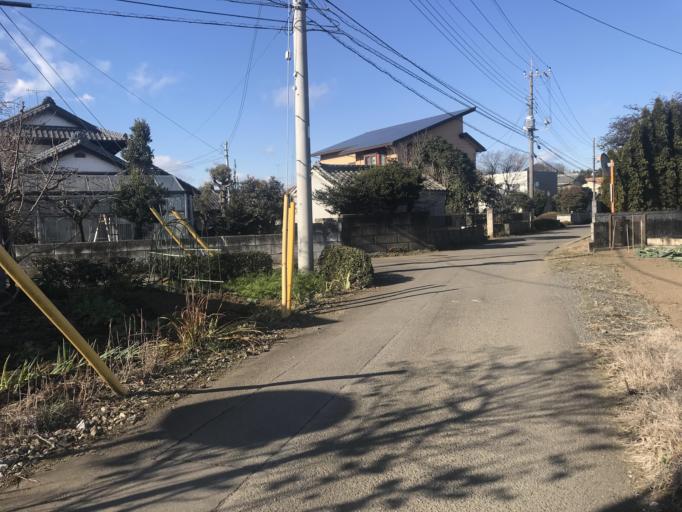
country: JP
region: Tochigi
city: Kaminokawa
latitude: 36.3909
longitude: 139.8739
